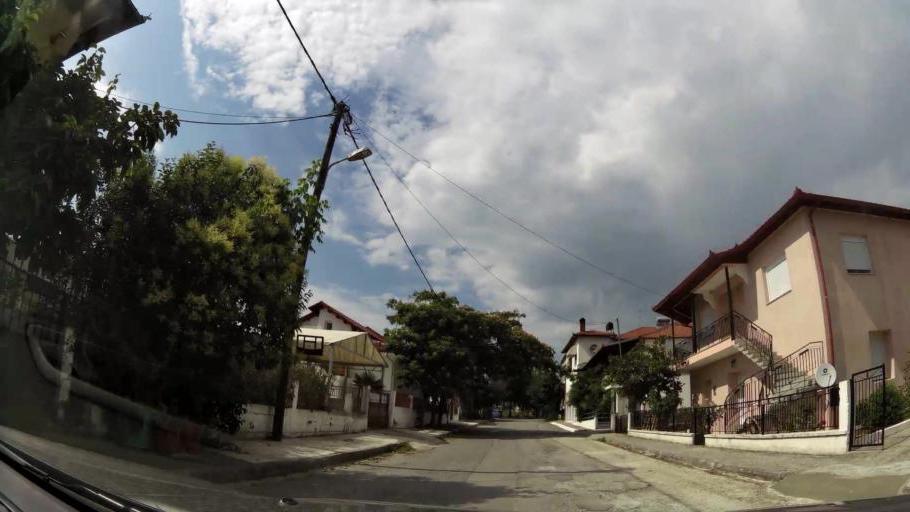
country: GR
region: Central Macedonia
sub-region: Nomos Pierias
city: Makrygialos
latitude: 40.4143
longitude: 22.6042
